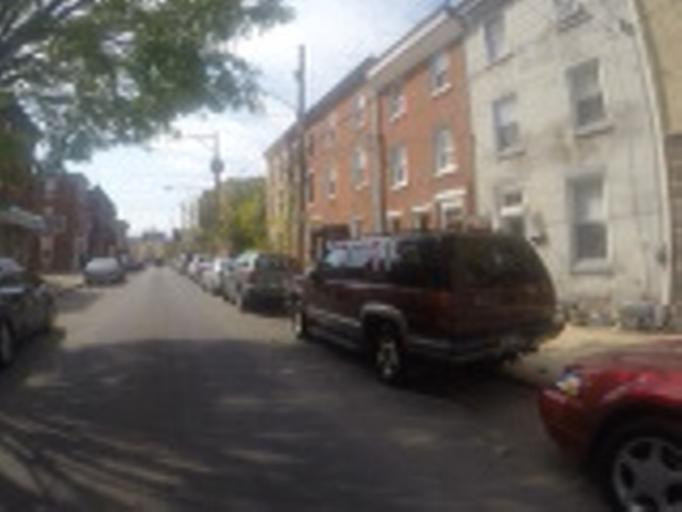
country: US
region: Pennsylvania
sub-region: Philadelphia County
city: Philadelphia
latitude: 39.9723
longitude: -75.1380
